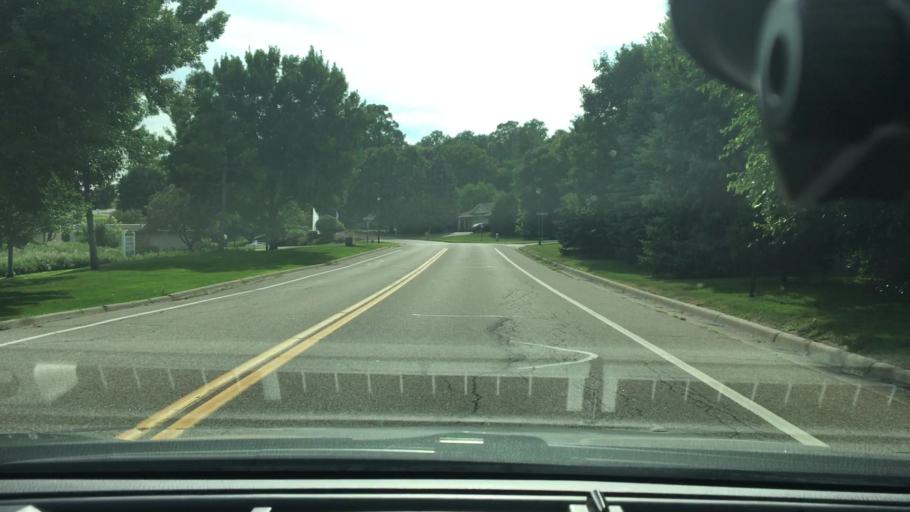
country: US
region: Minnesota
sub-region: Hennepin County
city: Plymouth
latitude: 44.9984
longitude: -93.4358
